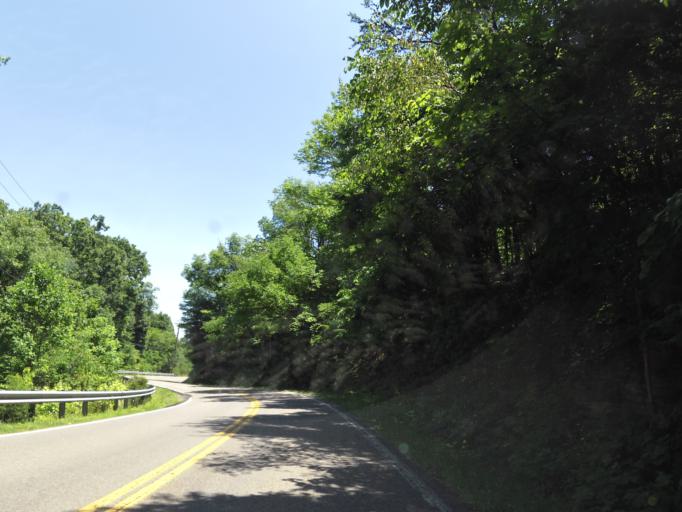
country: US
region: Tennessee
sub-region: Jefferson County
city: Dandridge
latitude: 35.9970
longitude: -83.3953
